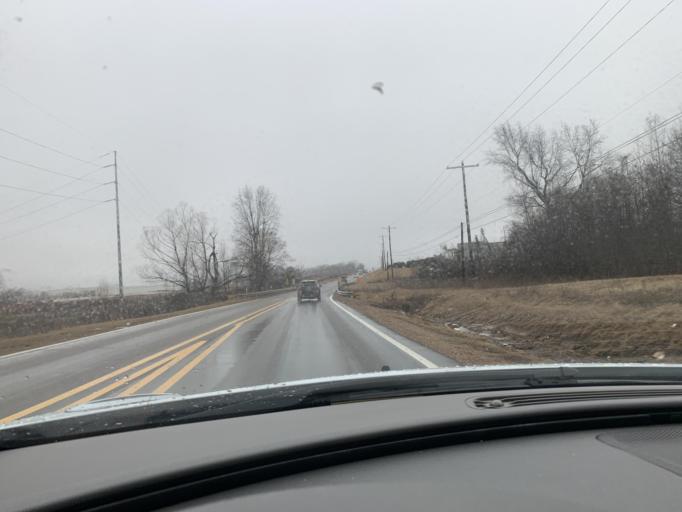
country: US
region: Mississippi
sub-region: De Soto County
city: Horn Lake
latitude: 34.9112
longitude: -90.0017
